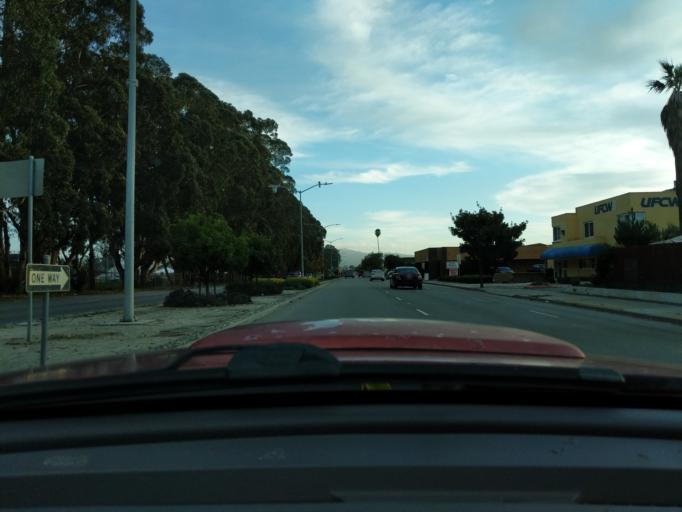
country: US
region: California
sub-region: Monterey County
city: Salinas
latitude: 36.6978
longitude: -121.6518
